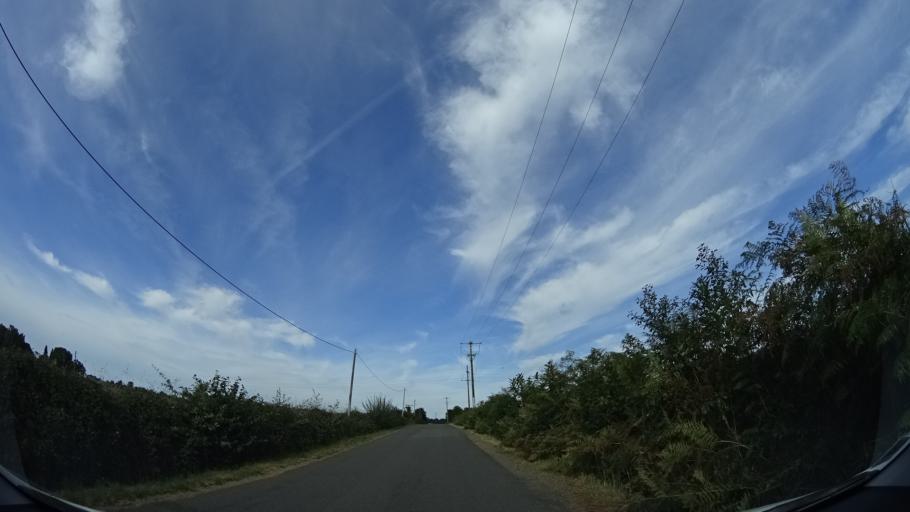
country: FR
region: Brittany
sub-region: Departement d'Ille-et-Vilaine
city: Romagne
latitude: 48.3234
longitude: -1.2698
